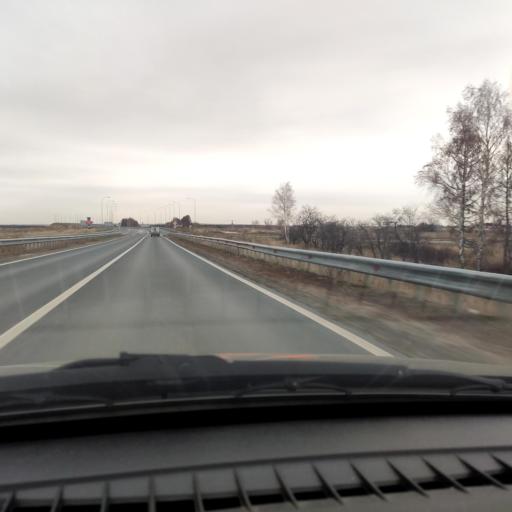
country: RU
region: Samara
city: Bereza
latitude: 53.4916
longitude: 50.1177
